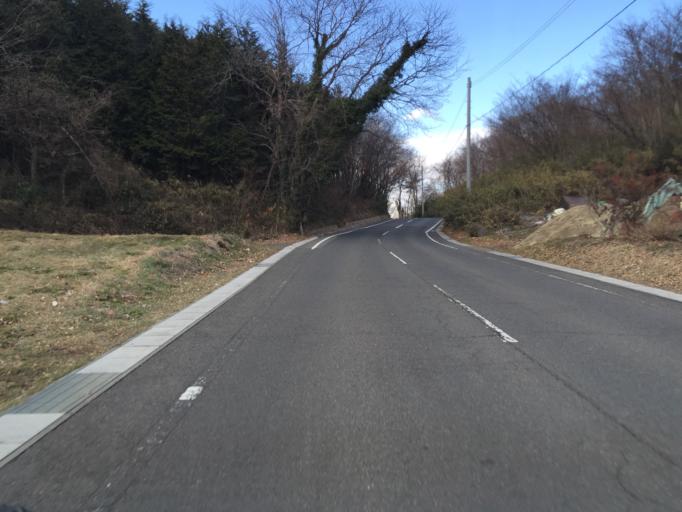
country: JP
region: Fukushima
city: Fukushima-shi
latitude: 37.6844
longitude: 140.4459
